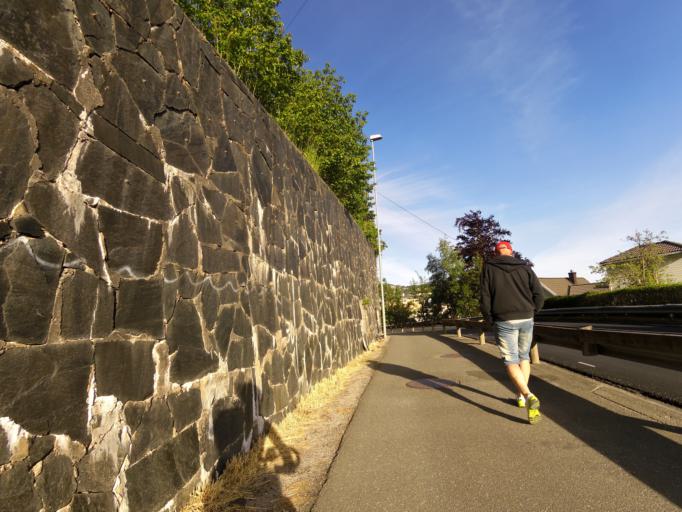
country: NO
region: Vest-Agder
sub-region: Flekkefjord
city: Flekkefjord
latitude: 58.2968
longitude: 6.6535
